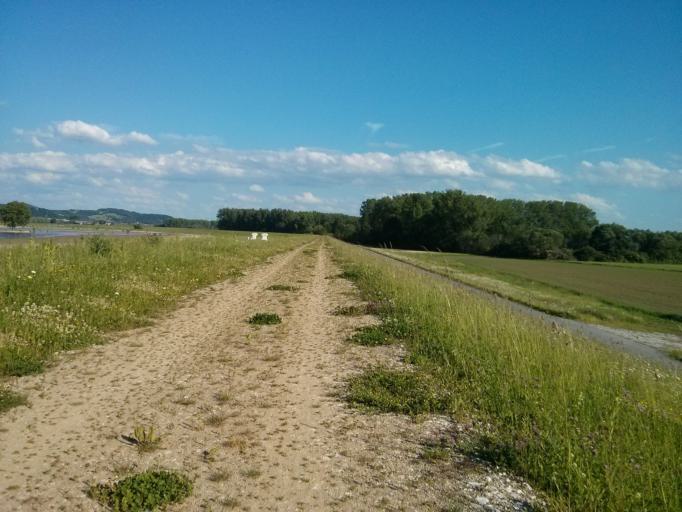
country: DE
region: Bavaria
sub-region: Lower Bavaria
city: Metten
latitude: 48.8373
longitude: 12.9152
